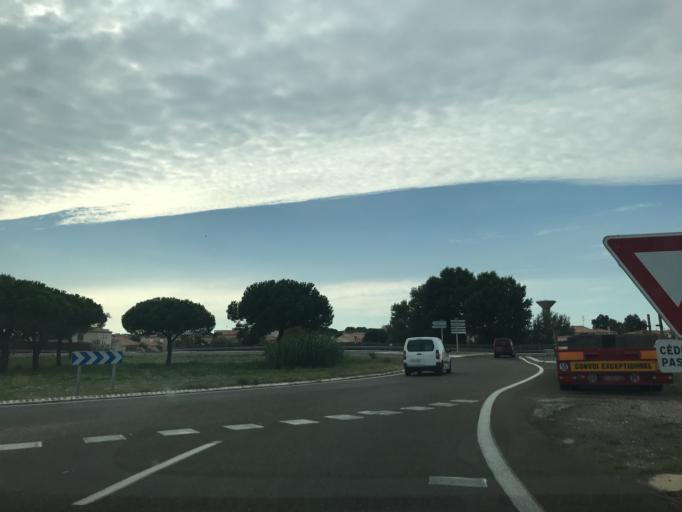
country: FR
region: Languedoc-Roussillon
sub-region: Departement du Gard
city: Le Grau-du-Roi
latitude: 43.5491
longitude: 4.1347
